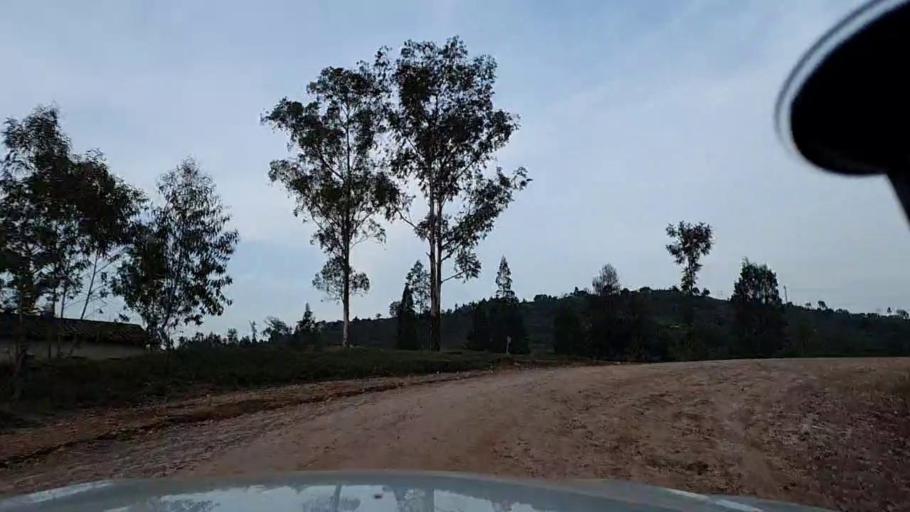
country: RW
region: Southern Province
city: Nyanza
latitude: -2.2259
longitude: 29.6542
